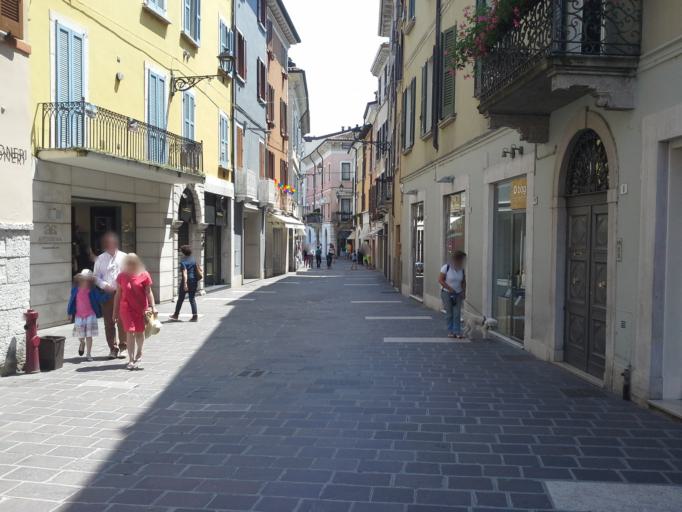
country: IT
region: Lombardy
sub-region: Provincia di Brescia
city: Desenzano del Garda
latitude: 45.4703
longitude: 10.5399
